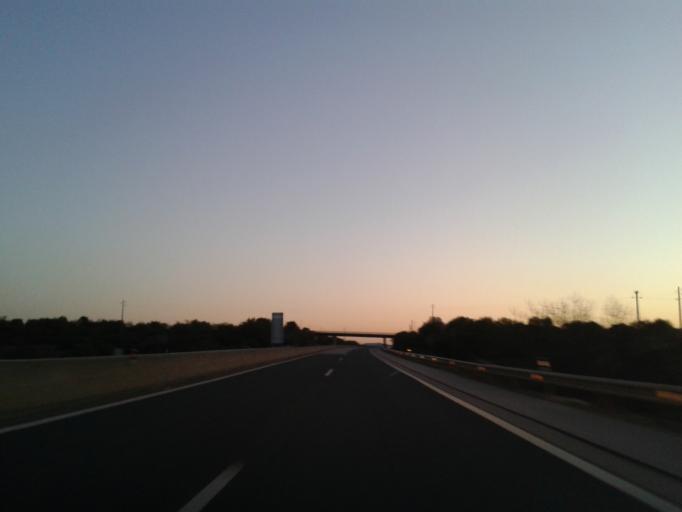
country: PT
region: Faro
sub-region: Albufeira
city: Ferreiras
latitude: 37.1400
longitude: -8.2299
